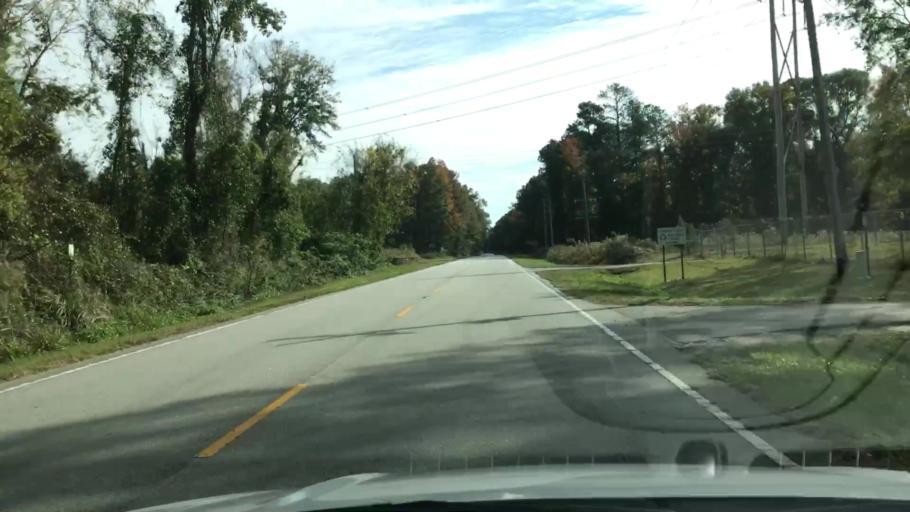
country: US
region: South Carolina
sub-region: Colleton County
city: Walterboro
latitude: 32.8018
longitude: -80.5048
